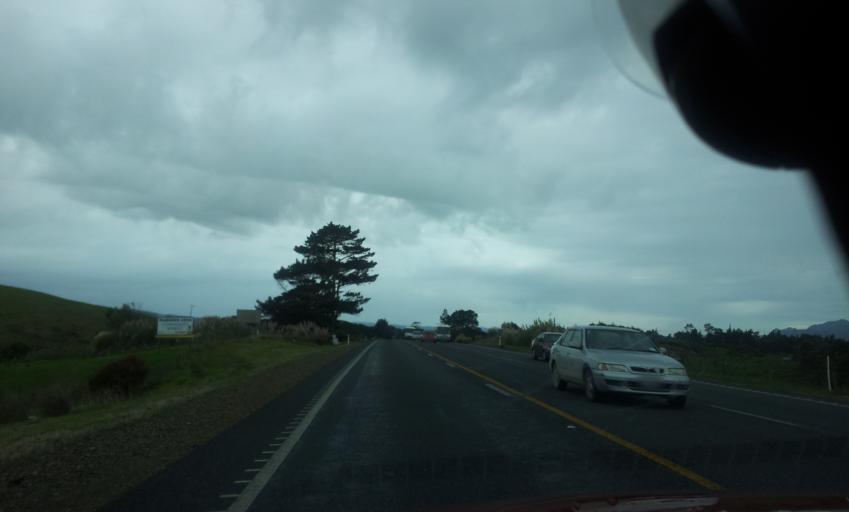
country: NZ
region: Northland
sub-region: Whangarei
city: Ruakaka
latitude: -35.9254
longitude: 174.4538
